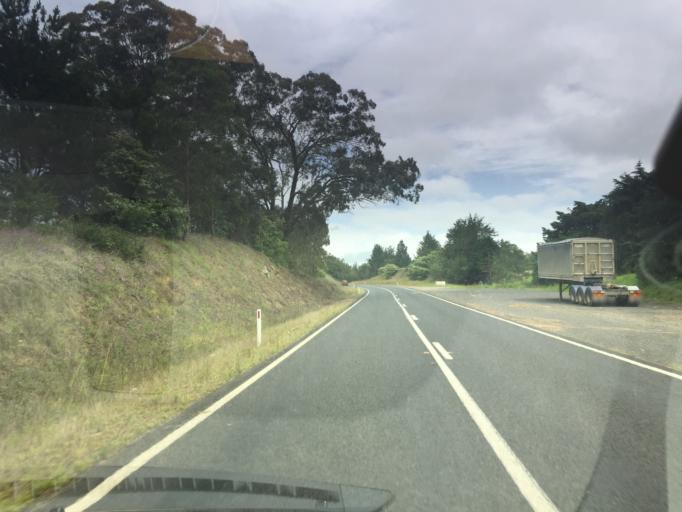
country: AU
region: New South Wales
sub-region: Bega Valley
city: Bega
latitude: -36.6413
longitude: 149.5835
